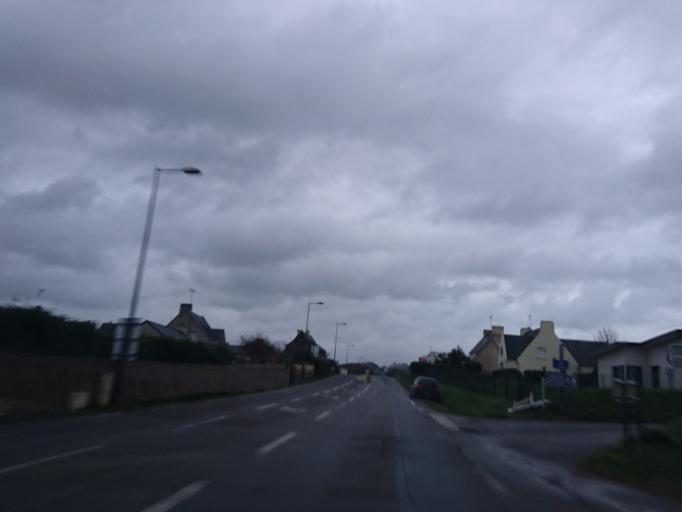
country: FR
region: Brittany
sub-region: Departement du Finistere
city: Le Conquet
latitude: 48.3594
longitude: -4.7626
